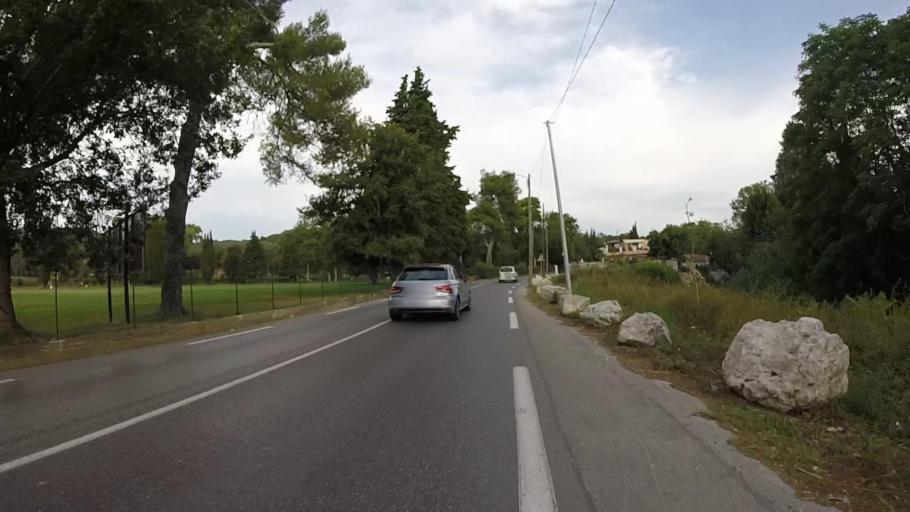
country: FR
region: Provence-Alpes-Cote d'Azur
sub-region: Departement des Alpes-Maritimes
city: Biot
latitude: 43.6170
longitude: 7.1047
